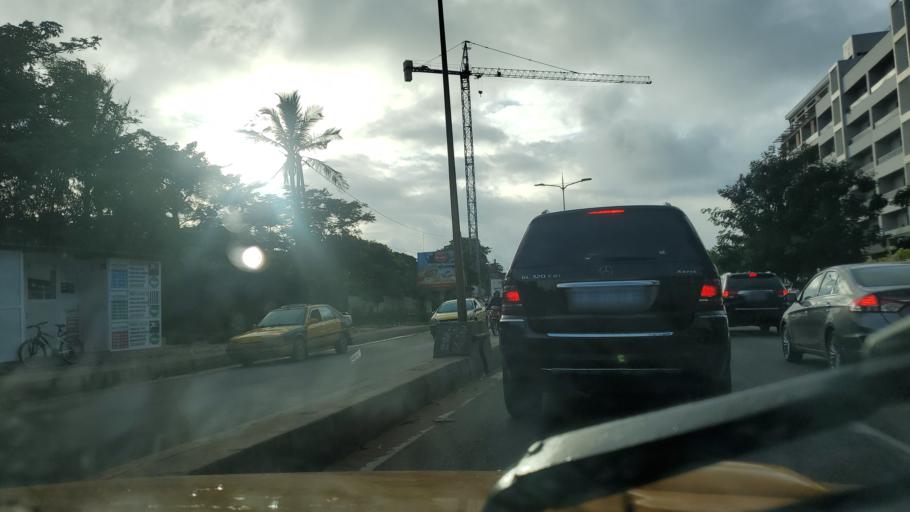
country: SN
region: Dakar
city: Mermoz Boabab
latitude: 14.7167
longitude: -17.4846
